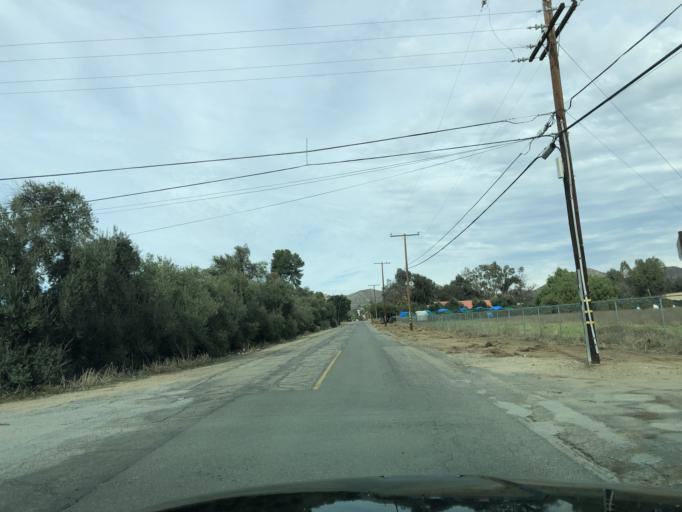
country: US
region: California
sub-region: Riverside County
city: Wildomar
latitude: 33.6159
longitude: -117.2712
